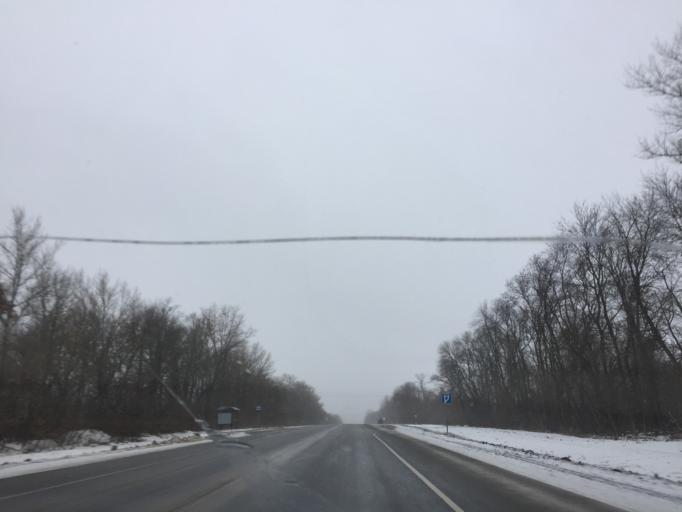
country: RU
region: Tula
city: Plavsk
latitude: 53.7339
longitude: 37.3103
